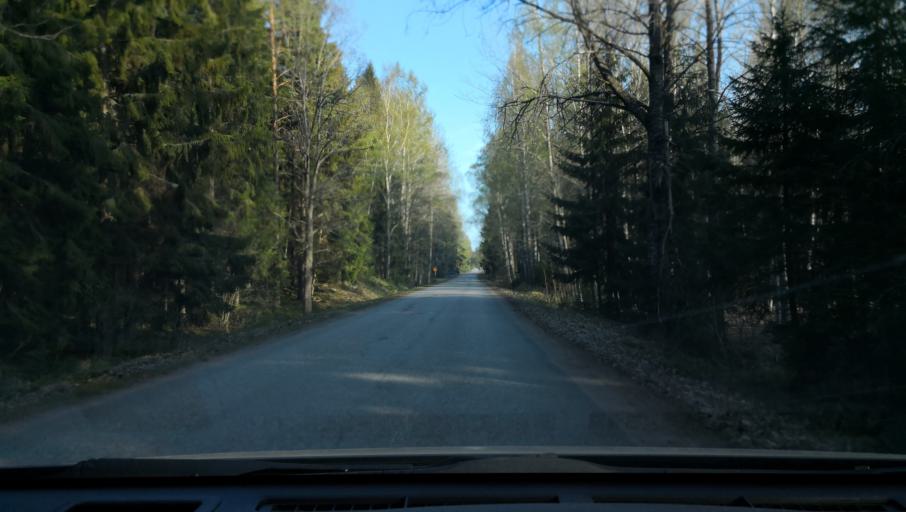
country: SE
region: Uppsala
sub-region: Heby Kommun
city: Tarnsjo
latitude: 60.2721
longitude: 16.9048
